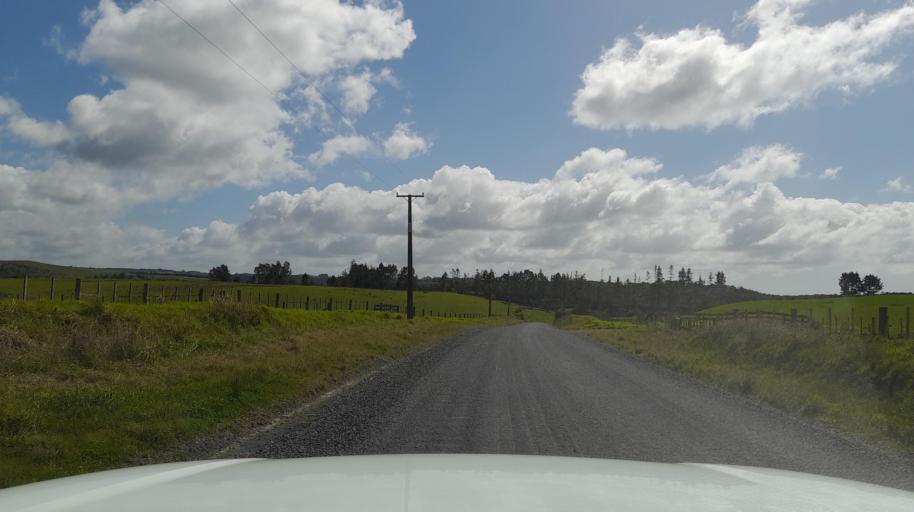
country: NZ
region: Northland
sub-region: Far North District
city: Kerikeri
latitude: -35.2208
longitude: 173.8706
